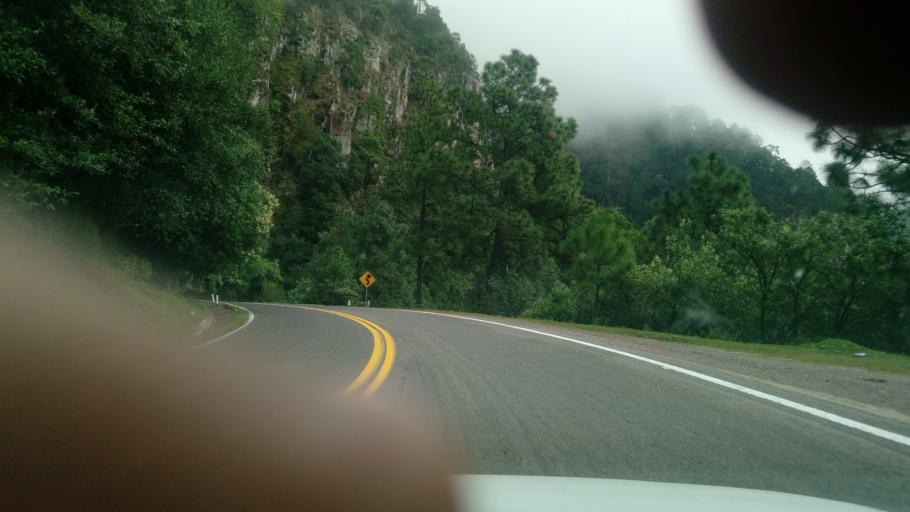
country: MX
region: Durango
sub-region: Pueblo Nuevo
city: La Ciudad
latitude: 23.6488
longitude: -105.7511
